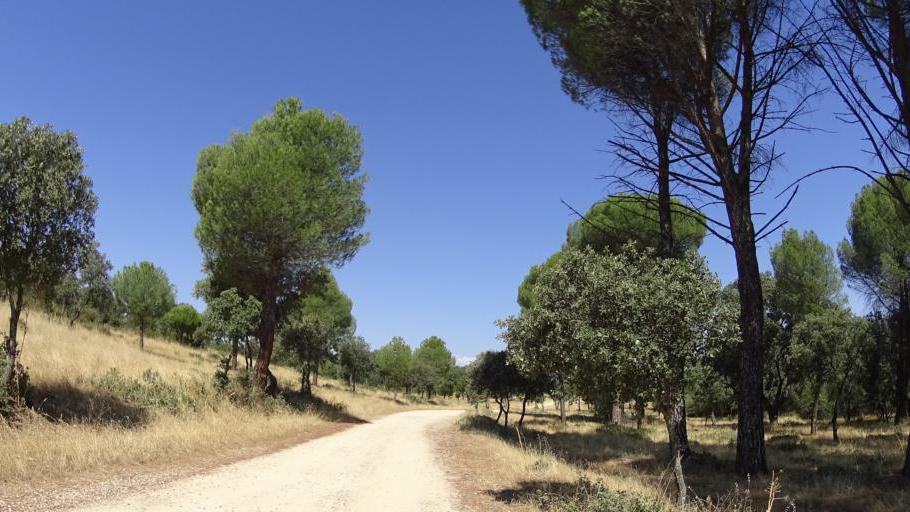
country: ES
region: Madrid
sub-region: Provincia de Madrid
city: Boadilla del Monte
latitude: 40.4285
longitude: -3.8544
